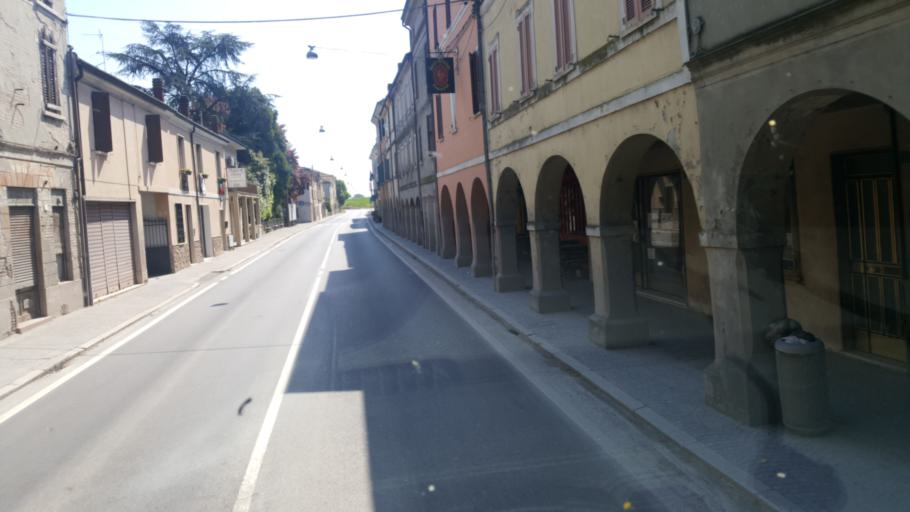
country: IT
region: Lombardy
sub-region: Provincia di Mantova
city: Sustinente
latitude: 45.0687
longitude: 11.0215
